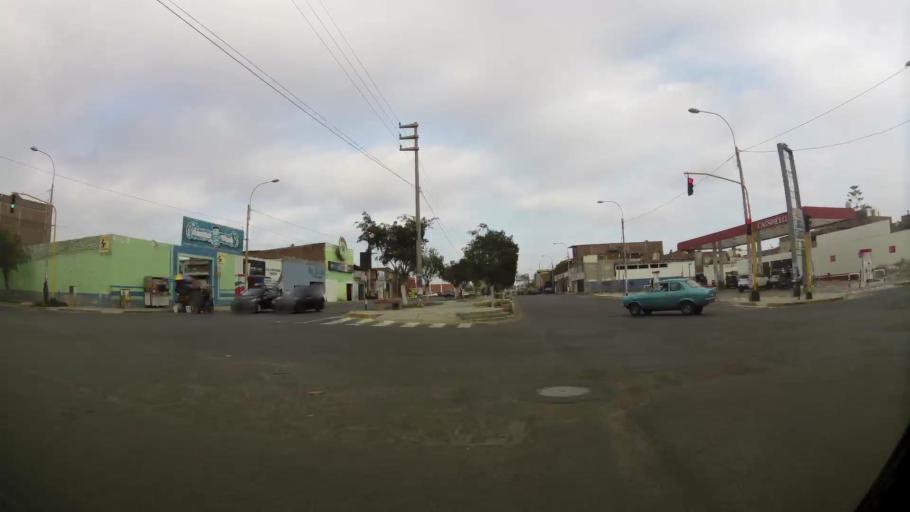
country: PE
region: La Libertad
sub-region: Provincia de Trujillo
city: Trujillo
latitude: -8.1007
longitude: -79.0265
